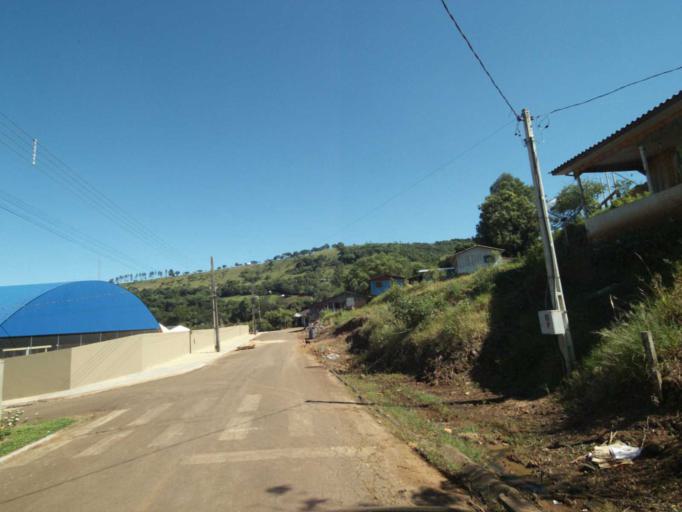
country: BR
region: Parana
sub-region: Francisco Beltrao
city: Francisco Beltrao
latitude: -26.1451
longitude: -53.3063
